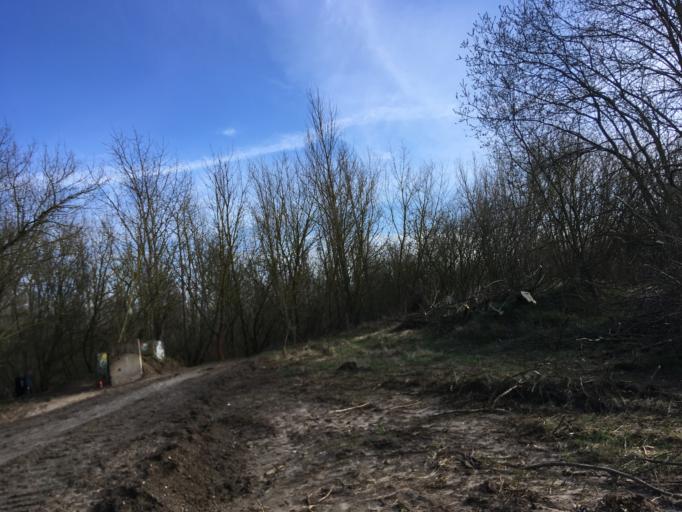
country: DE
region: Berlin
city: Blankenfelde
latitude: 52.6338
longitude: 13.4110
